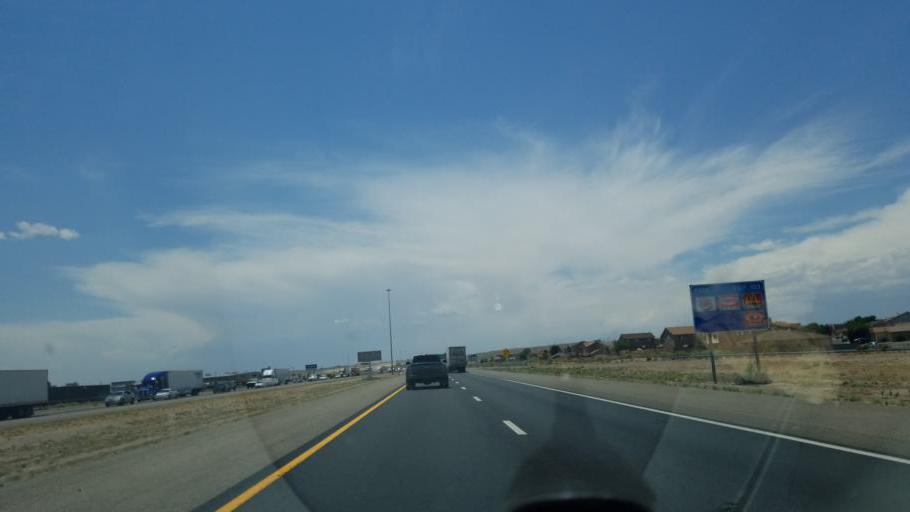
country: US
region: New Mexico
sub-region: Bernalillo County
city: Albuquerque
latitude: 35.0931
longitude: -106.7330
